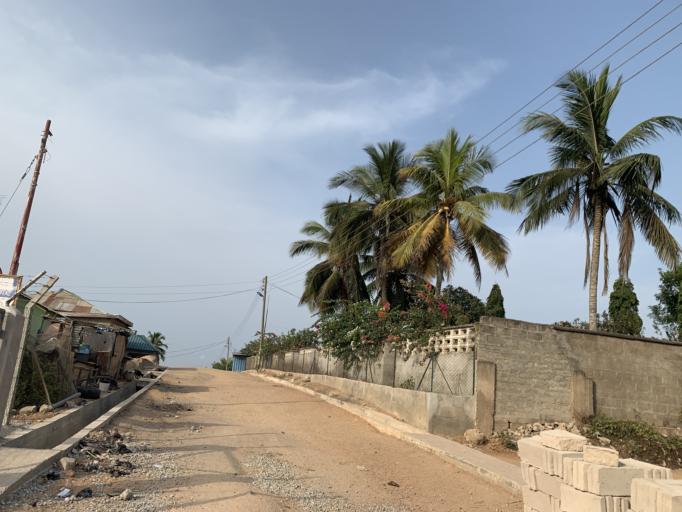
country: GH
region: Central
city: Winneba
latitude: 5.3361
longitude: -0.6235
